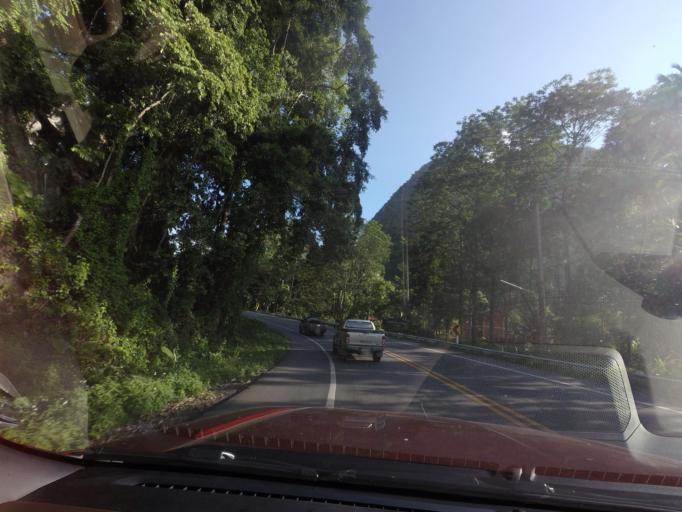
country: TH
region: Yala
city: Than To
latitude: 6.2151
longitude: 101.1661
